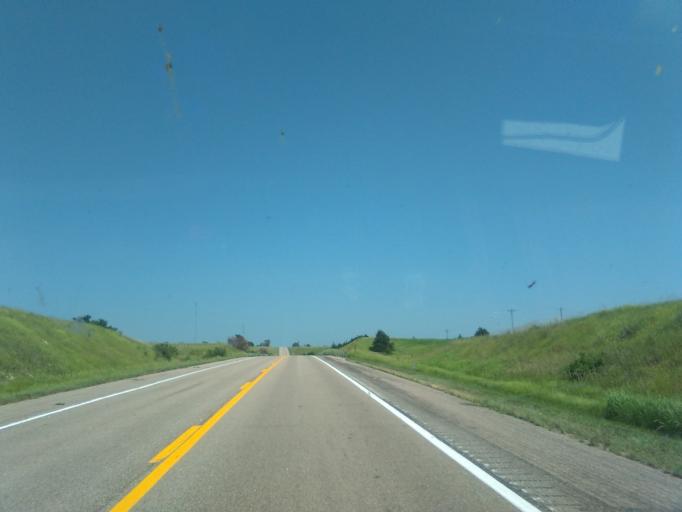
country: US
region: Nebraska
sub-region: Frontier County
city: Stockville
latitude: 40.5882
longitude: -100.6295
